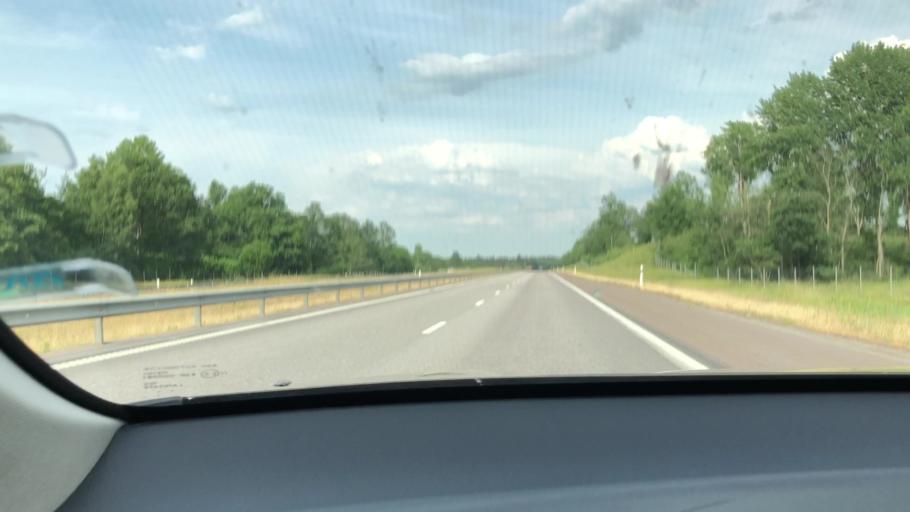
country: SE
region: OEstergoetland
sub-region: Boxholms Kommun
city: Boxholm
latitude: 58.3027
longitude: 14.9638
